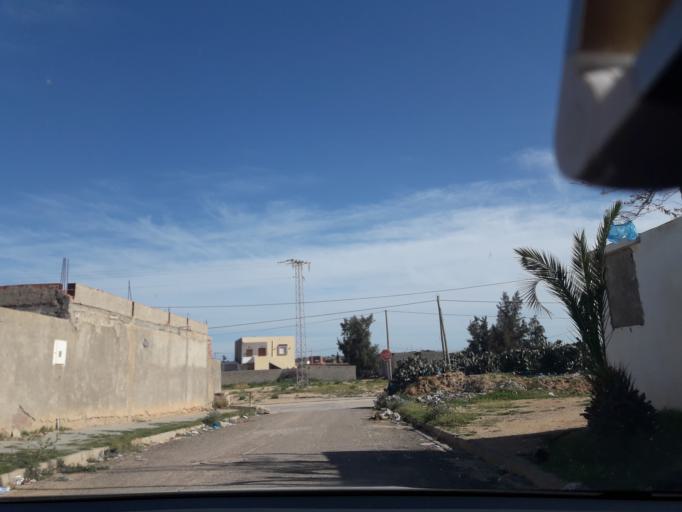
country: TN
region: Safaqis
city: Sfax
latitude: 34.7367
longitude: 10.5220
